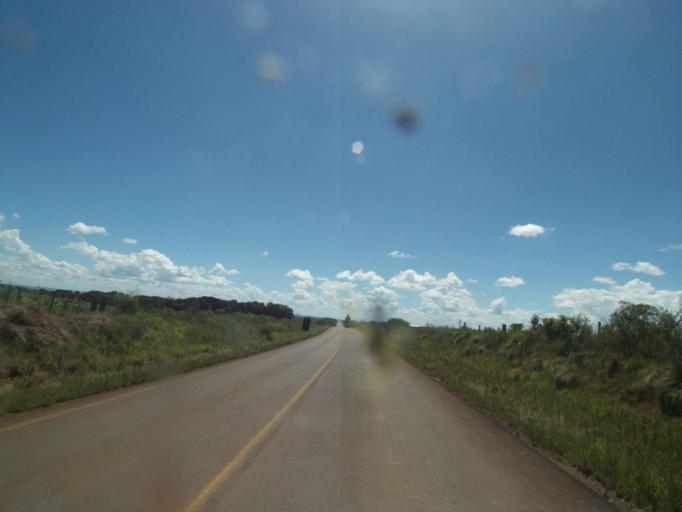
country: BR
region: Parana
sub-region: Pinhao
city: Pinhao
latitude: -25.8133
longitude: -52.0468
